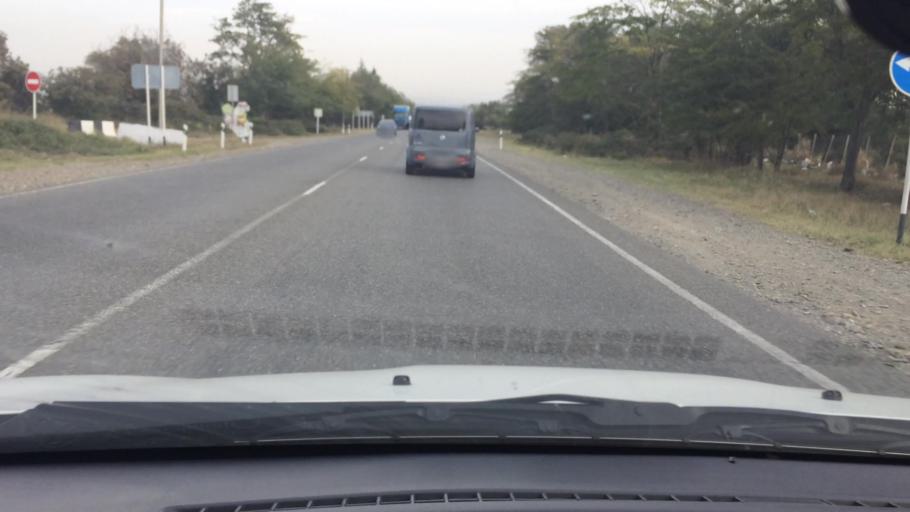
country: GE
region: T'bilisi
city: Tbilisi
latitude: 41.6427
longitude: 44.8559
